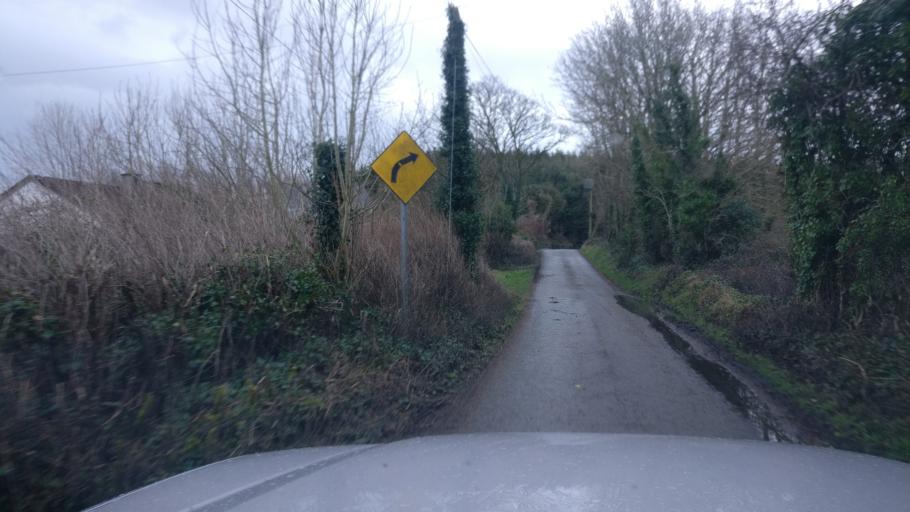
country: IE
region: Connaught
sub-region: County Galway
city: Athenry
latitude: 53.1868
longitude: -8.6951
